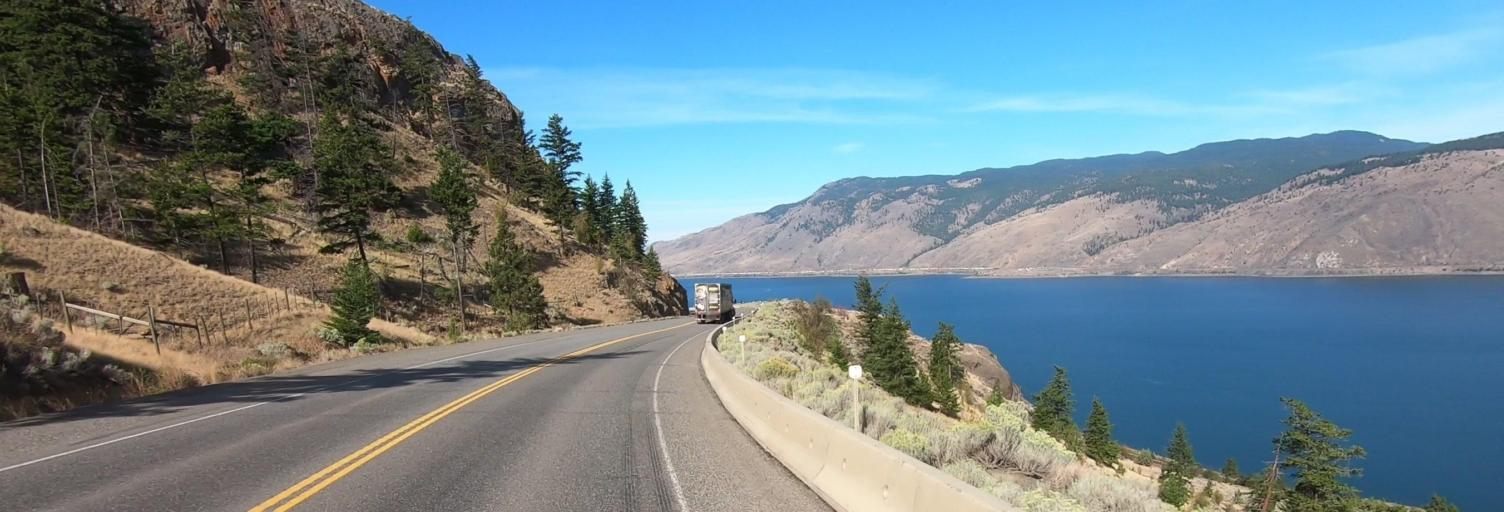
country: CA
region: British Columbia
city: Logan Lake
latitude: 50.7659
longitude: -120.7614
